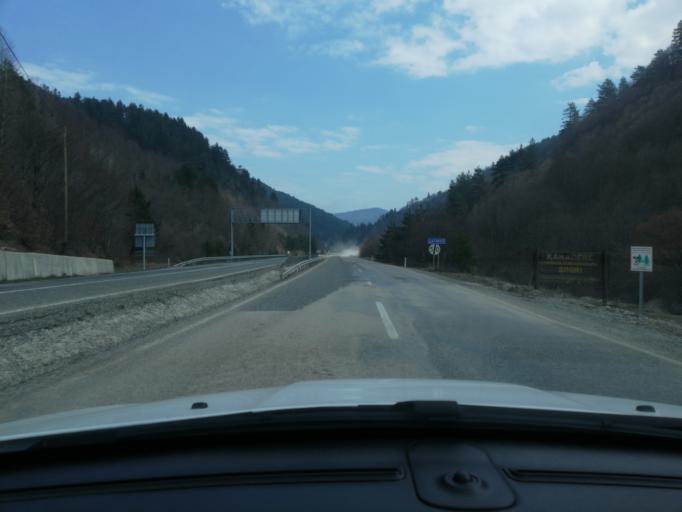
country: TR
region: Kastamonu
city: Kuzyaka
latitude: 41.1437
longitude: 33.7798
